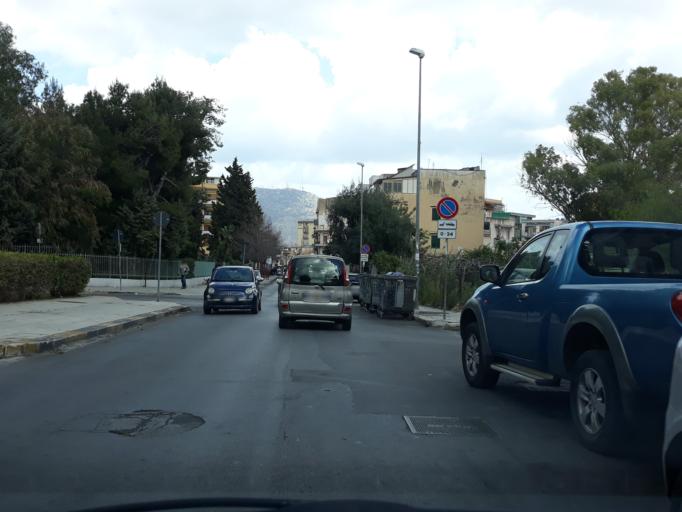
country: IT
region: Sicily
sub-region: Palermo
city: Palermo
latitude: 38.1239
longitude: 13.3106
